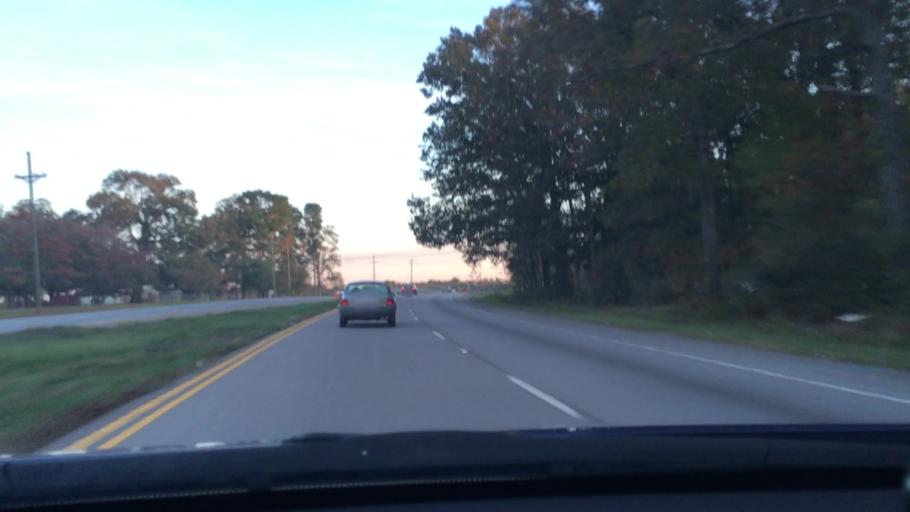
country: US
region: South Carolina
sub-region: Richland County
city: Hopkins
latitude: 33.9462
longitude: -80.8080
